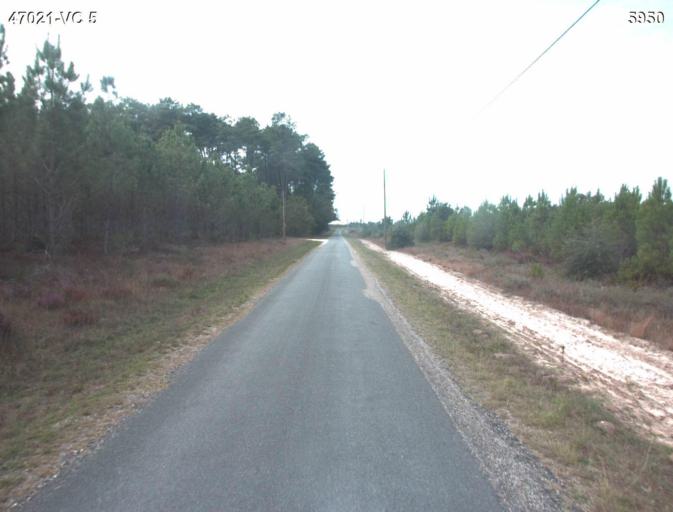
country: FR
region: Aquitaine
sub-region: Departement du Lot-et-Garonne
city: Barbaste
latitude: 44.1495
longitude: 0.2270
